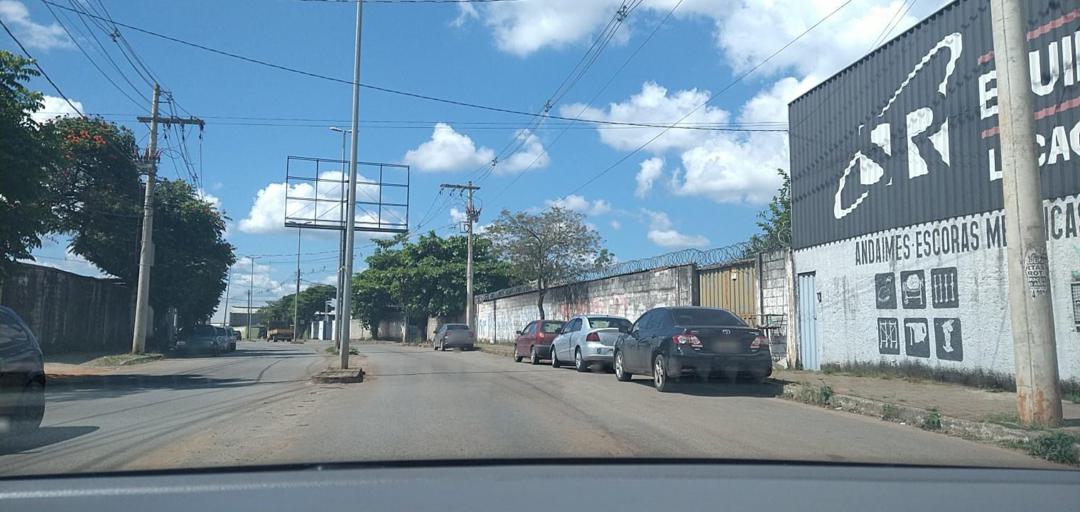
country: BR
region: Minas Gerais
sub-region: Joao Monlevade
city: Joao Monlevade
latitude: -19.8315
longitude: -43.1881
